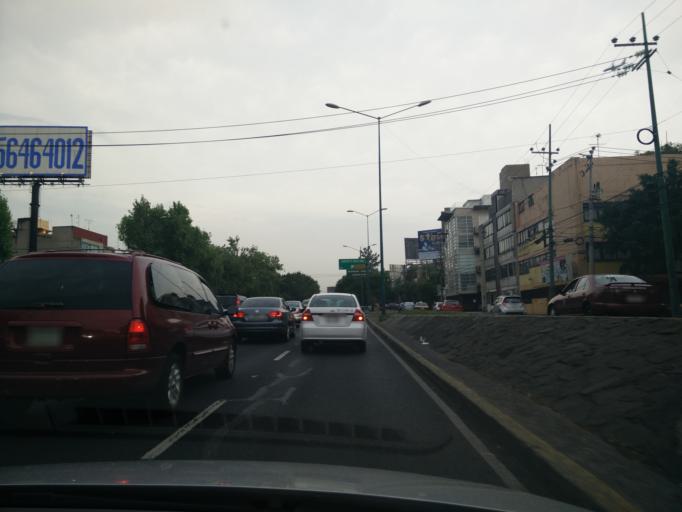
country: MX
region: Mexico City
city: Colonia Nativitas
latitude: 19.4032
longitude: -99.1355
